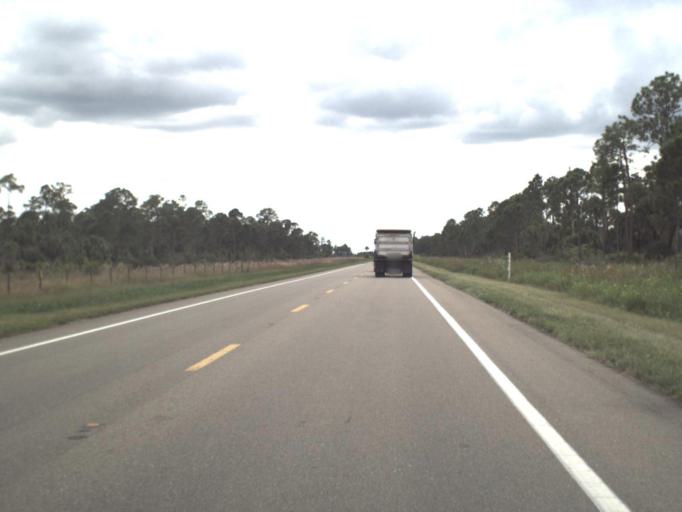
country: US
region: Florida
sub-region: Lee County
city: Olga
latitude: 26.9005
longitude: -81.7602
